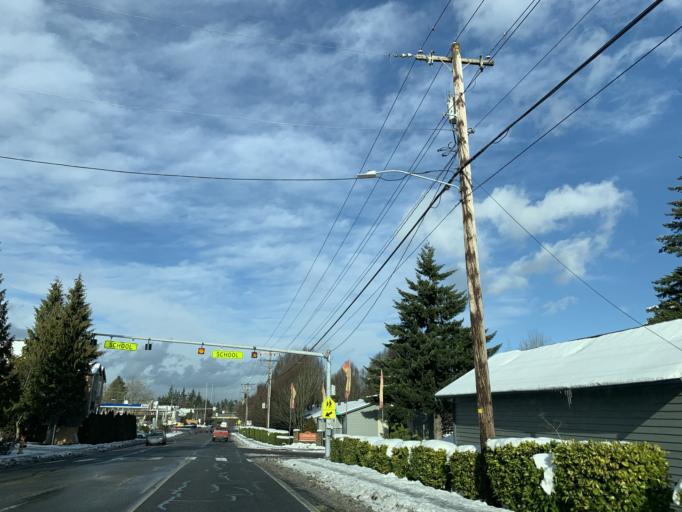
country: US
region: Washington
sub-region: Snohomish County
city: Mukilteo
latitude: 47.9201
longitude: -122.2404
